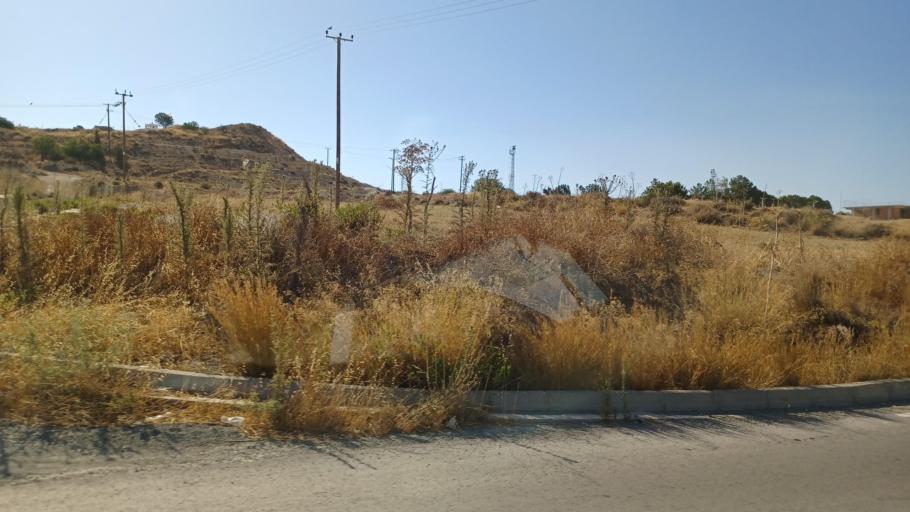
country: CY
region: Larnaka
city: Pyla
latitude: 35.0001
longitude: 33.6921
